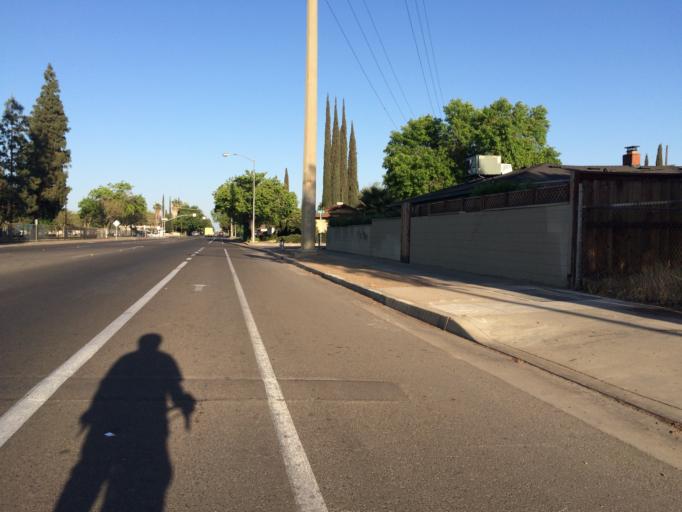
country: US
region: California
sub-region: Fresno County
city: Fresno
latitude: 36.7868
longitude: -119.7840
